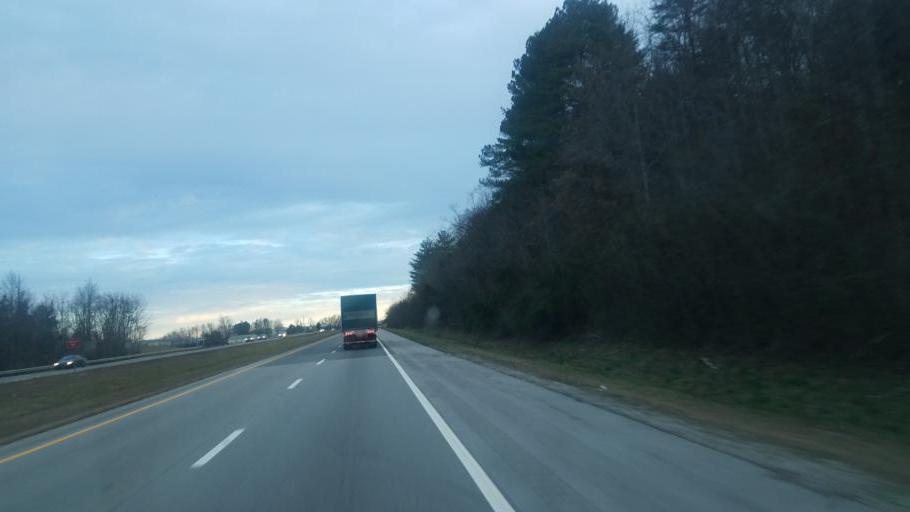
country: US
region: Tennessee
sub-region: Putnam County
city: Cookeville
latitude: 36.1098
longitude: -85.4994
